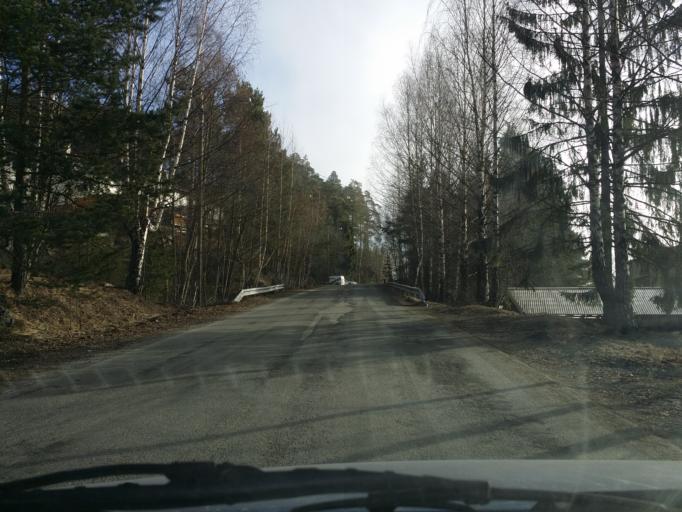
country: NO
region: Buskerud
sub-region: Nedre Eiker
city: Mjondalen
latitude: 59.7625
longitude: 10.0331
